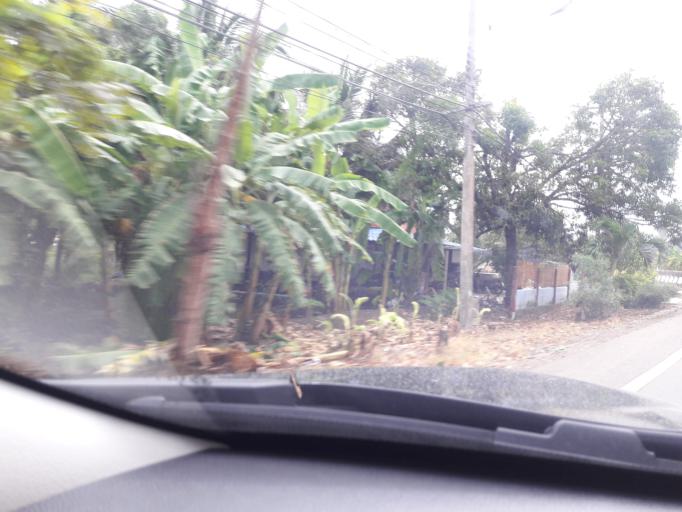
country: TH
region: Ratchaburi
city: Damnoen Saduak
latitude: 13.5279
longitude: 99.9593
